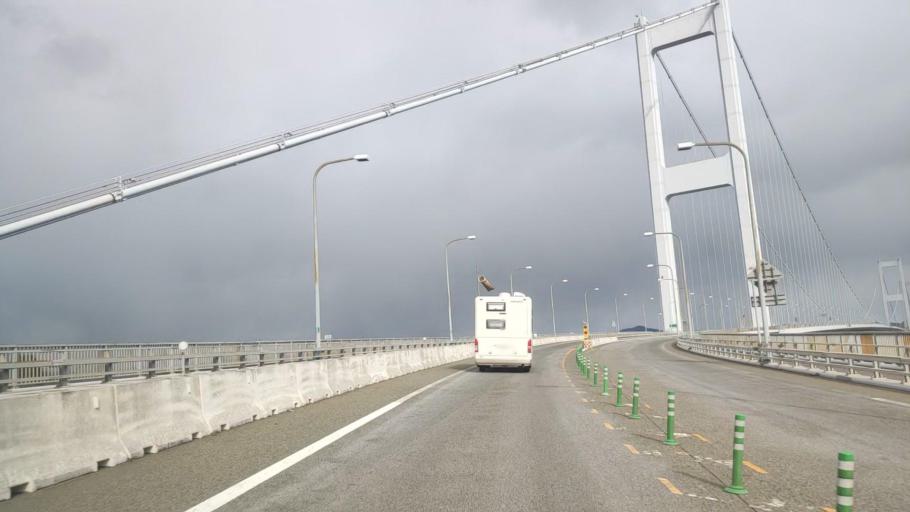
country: JP
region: Hiroshima
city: Takehara
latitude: 34.1118
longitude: 132.9773
